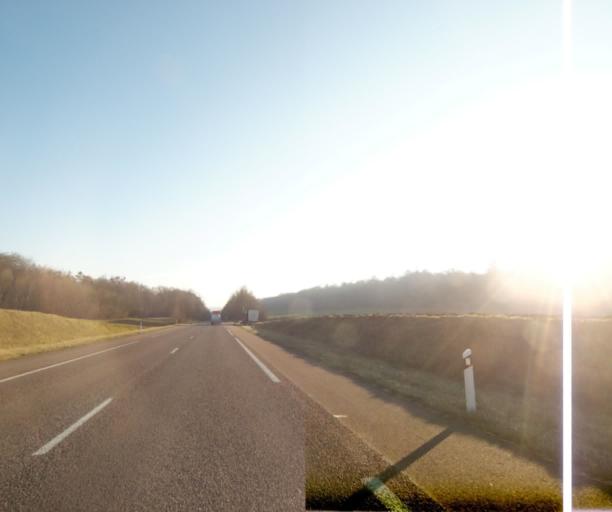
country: FR
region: Champagne-Ardenne
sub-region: Departement de la Haute-Marne
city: Chevillon
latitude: 48.4945
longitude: 5.1103
